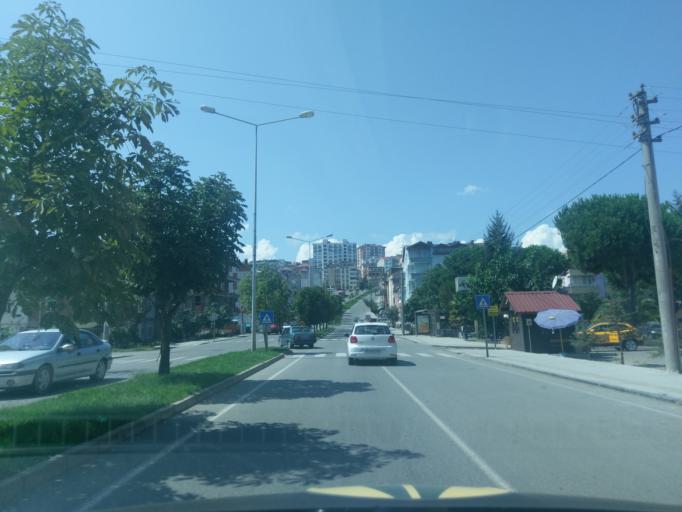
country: TR
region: Ordu
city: Ordu
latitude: 40.9662
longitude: 37.9040
